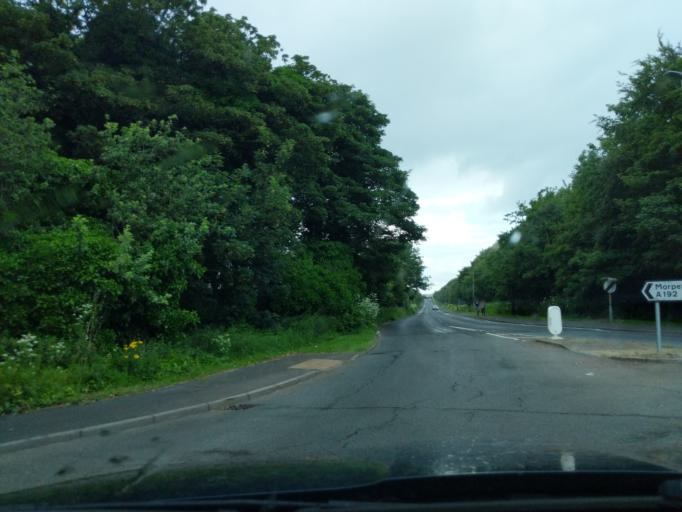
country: GB
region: England
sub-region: Northumberland
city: Seaton Delaval
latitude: 55.0773
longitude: -1.5413
